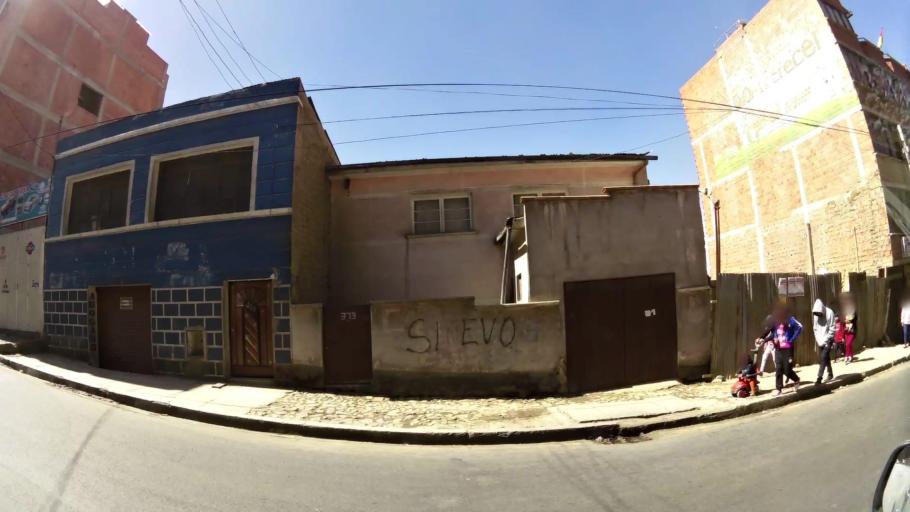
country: BO
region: La Paz
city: La Paz
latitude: -16.4904
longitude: -68.1666
